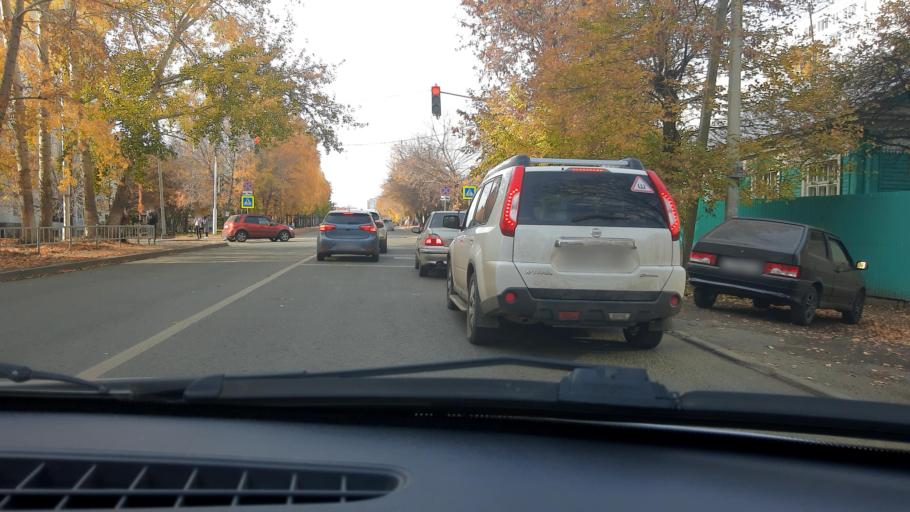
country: RU
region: Bashkortostan
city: Ufa
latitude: 54.7569
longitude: 56.0194
